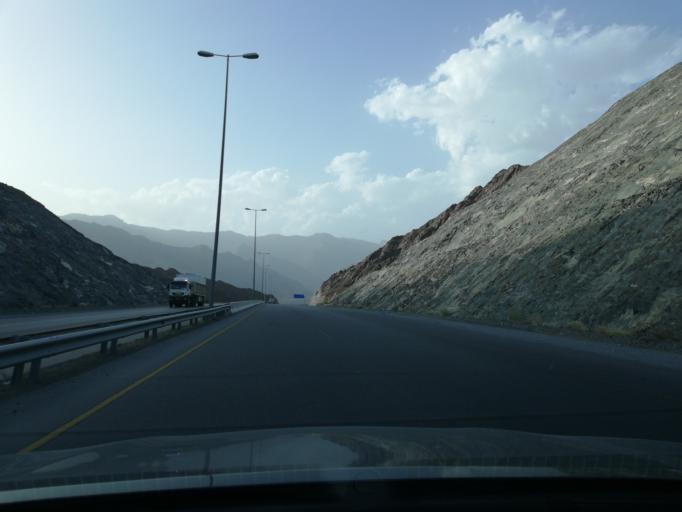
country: OM
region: Muhafazat ad Dakhiliyah
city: Izki
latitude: 22.9630
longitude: 57.7852
